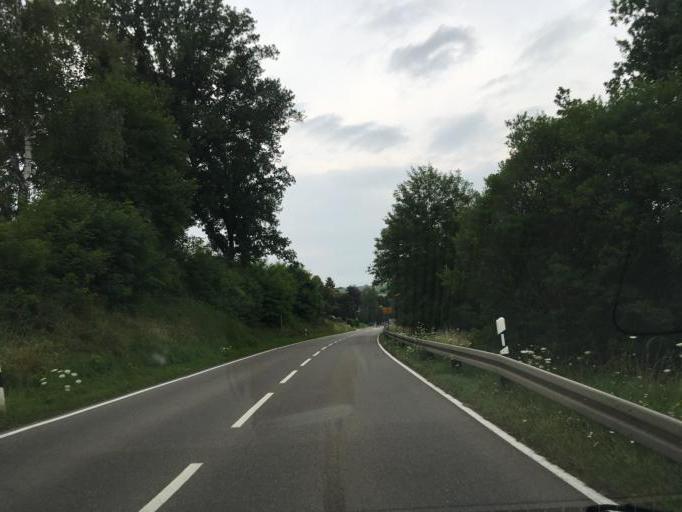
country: DE
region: Baden-Wuerttemberg
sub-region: Regierungsbezirk Stuttgart
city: Waldenbuch
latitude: 48.6301
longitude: 9.1316
